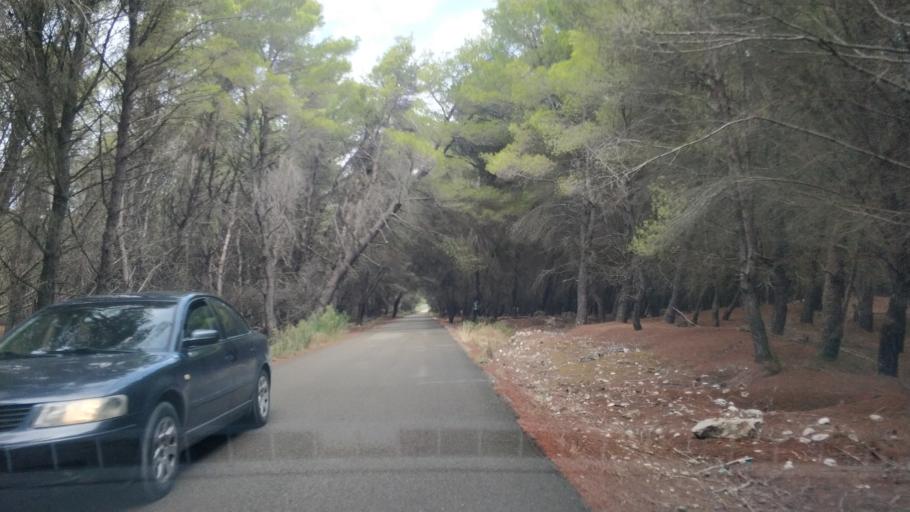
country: AL
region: Vlore
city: Vlore
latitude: 40.4978
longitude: 19.4313
